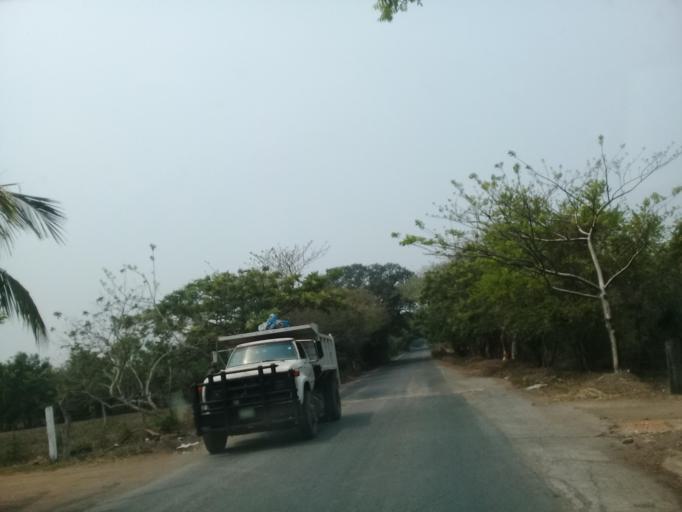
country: MX
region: Veracruz
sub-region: Medellin
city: La Laguna y Monte del Castillo
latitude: 18.9606
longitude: -96.1215
